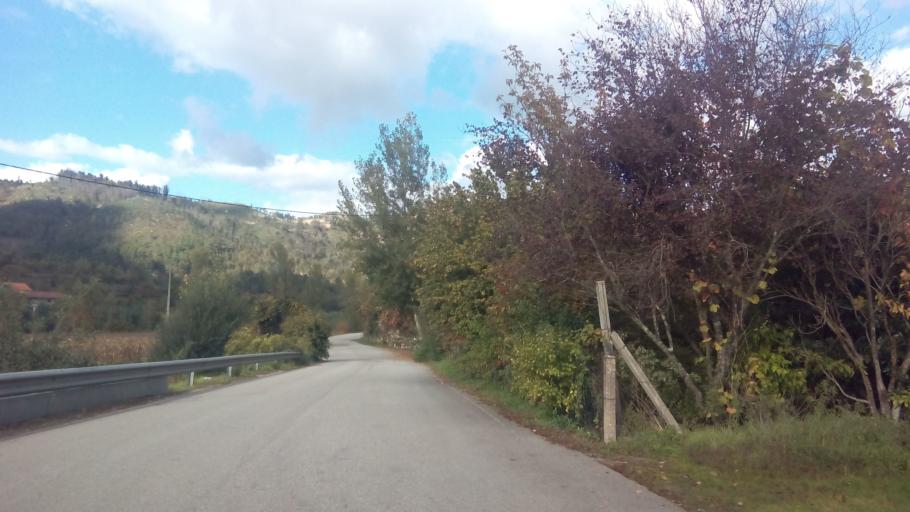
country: PT
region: Porto
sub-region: Amarante
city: Amarante
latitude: 41.2813
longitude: -7.9923
